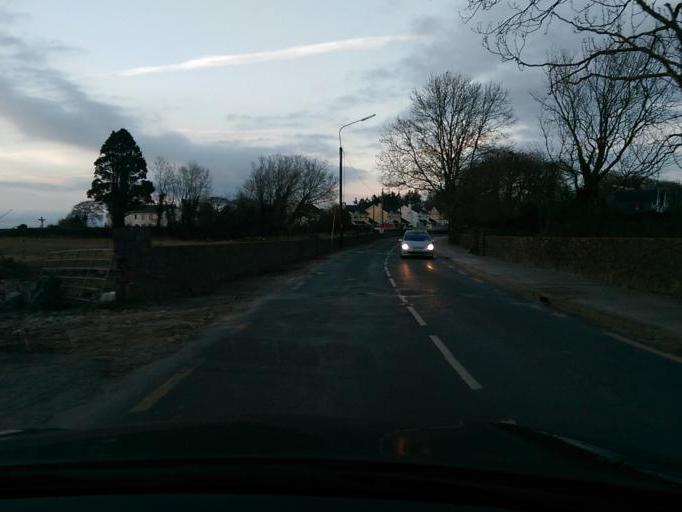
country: IE
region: Munster
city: Nenagh Bridge
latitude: 52.9889
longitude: -8.1324
